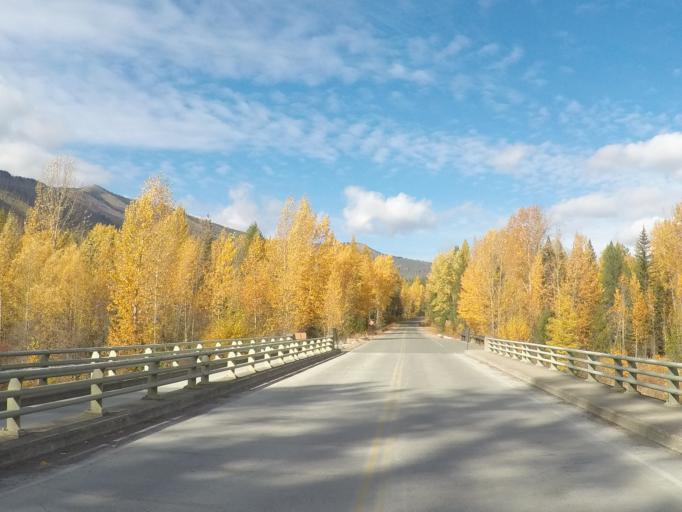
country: US
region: Montana
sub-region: Flathead County
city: Columbia Falls
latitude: 48.5259
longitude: -113.9966
